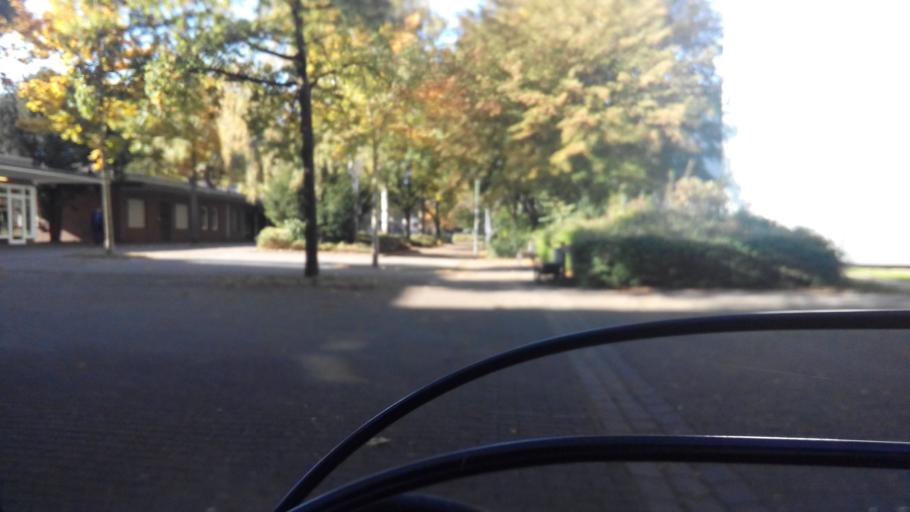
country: DE
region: North Rhine-Westphalia
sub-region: Regierungsbezirk Munster
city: Gelsenkirchen
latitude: 51.4984
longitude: 7.1347
